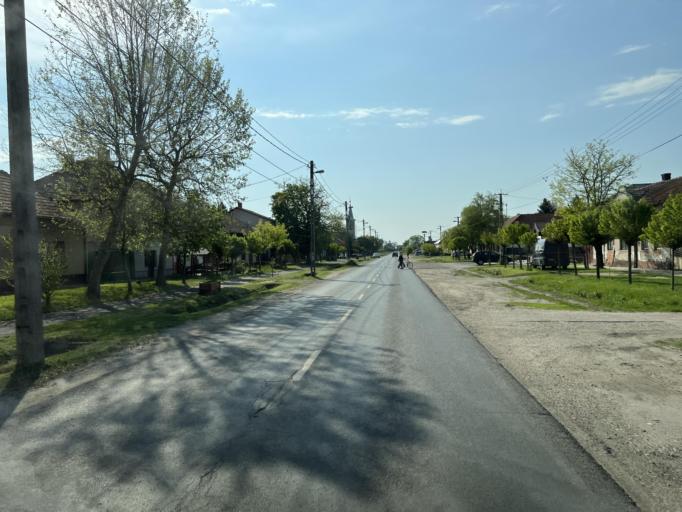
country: HU
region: Pest
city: Jaszkarajeno
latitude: 47.0525
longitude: 20.0683
